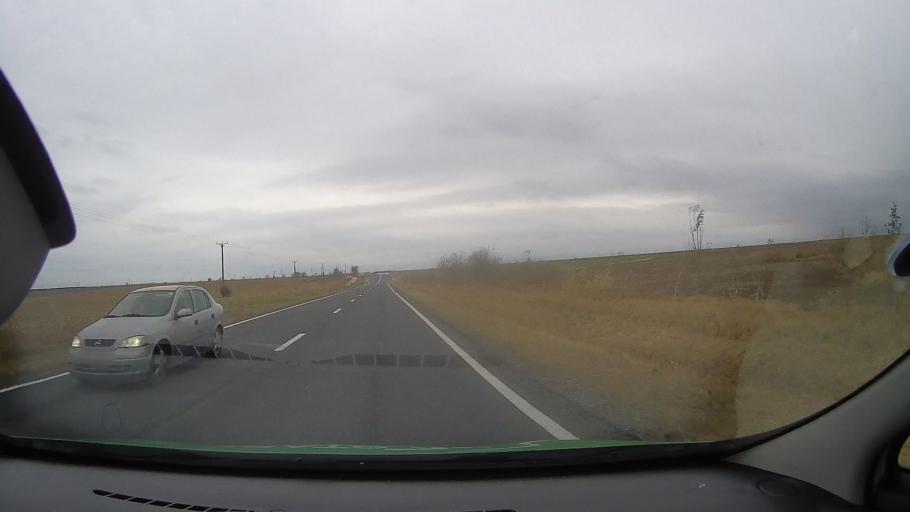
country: RO
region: Constanta
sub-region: Comuna Nicolae Balcescu
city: Nicolae Balcescu
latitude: 44.3837
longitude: 28.3976
